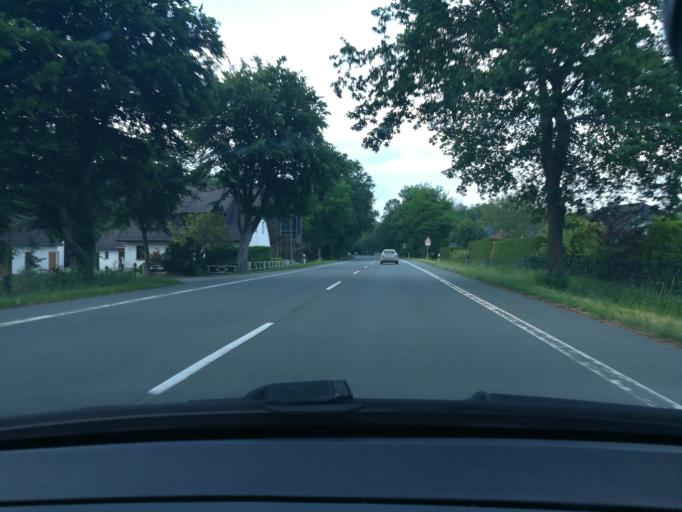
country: DE
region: North Rhine-Westphalia
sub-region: Regierungsbezirk Detmold
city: Augustdorf
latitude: 51.8797
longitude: 8.6748
